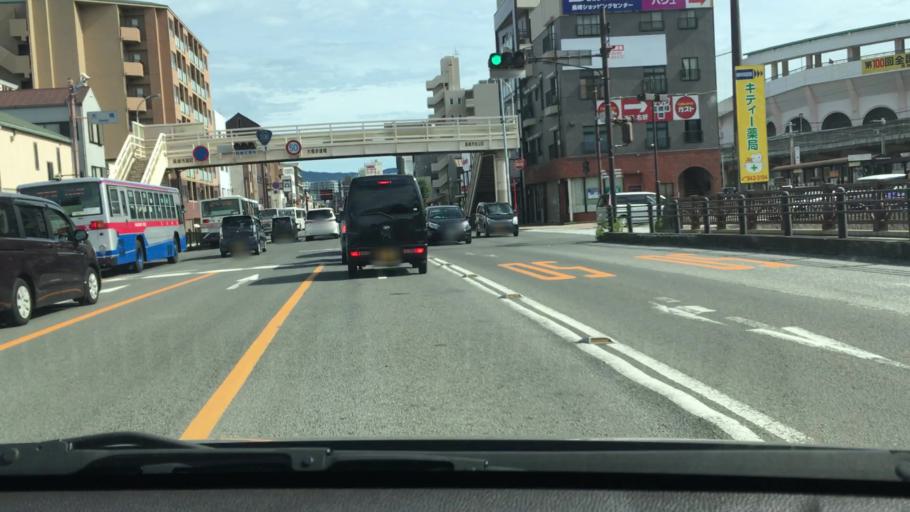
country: JP
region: Nagasaki
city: Nagasaki-shi
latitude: 32.7786
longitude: 129.8618
